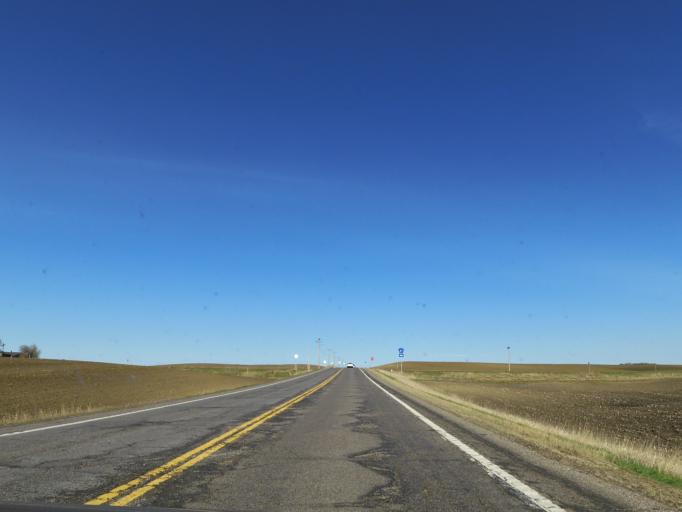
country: US
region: Minnesota
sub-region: Scott County
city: Elko New Market
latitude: 44.5730
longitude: -93.3809
